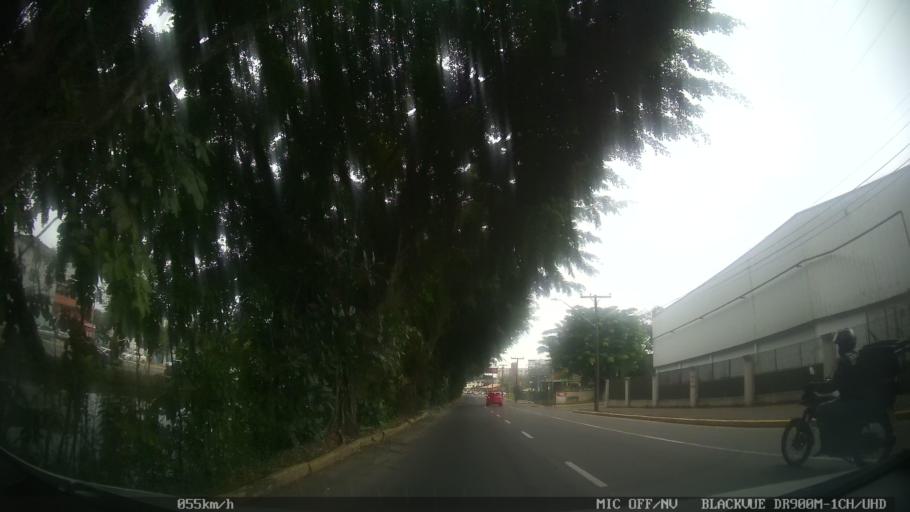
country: BR
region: Santa Catarina
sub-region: Joinville
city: Joinville
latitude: -26.2971
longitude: -48.8420
